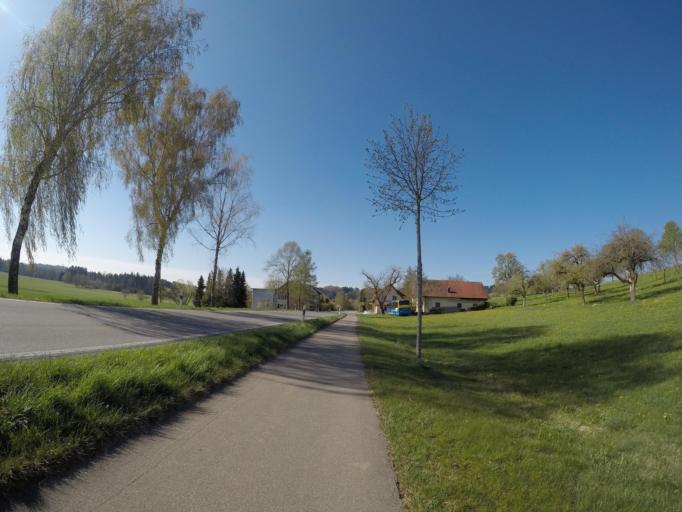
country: DE
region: Baden-Wuerttemberg
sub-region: Tuebingen Region
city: Ebenweiler
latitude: 47.8857
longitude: 9.5187
